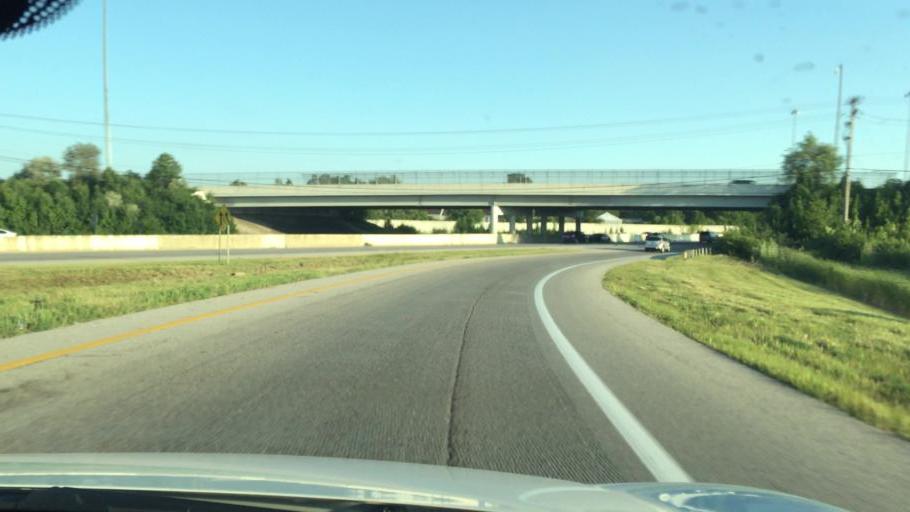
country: US
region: Ohio
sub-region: Franklin County
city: Worthington
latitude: 40.1065
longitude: -82.9813
